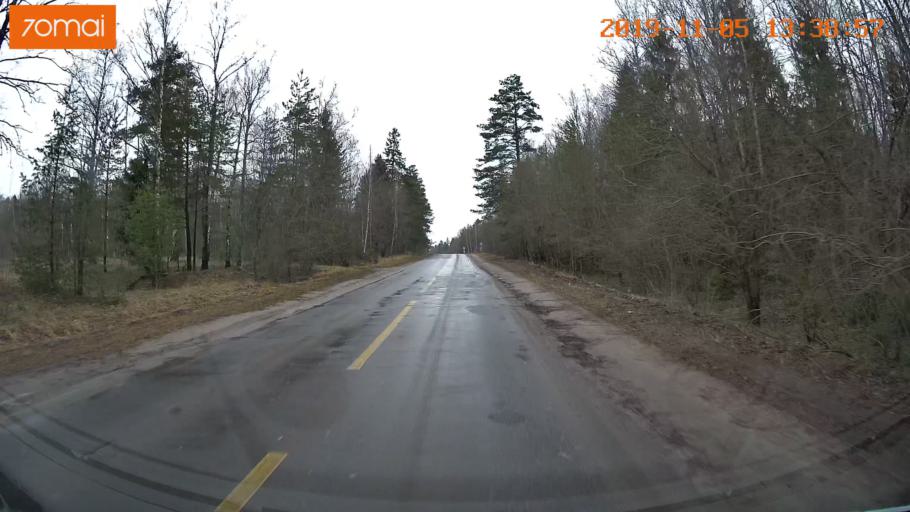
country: RU
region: Ivanovo
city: Shuya
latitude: 56.9358
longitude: 41.3869
